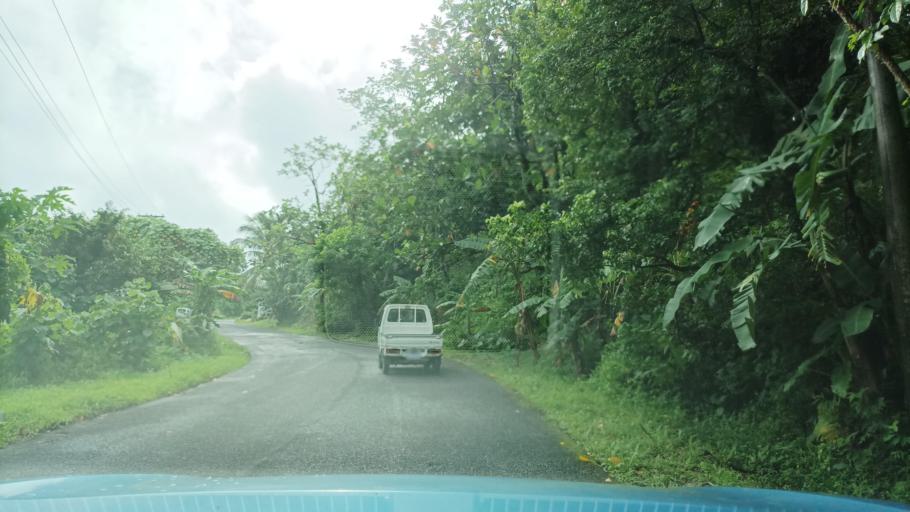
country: FM
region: Pohnpei
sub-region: Kolonia Municipality
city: Kolonia
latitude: 6.9694
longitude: 158.2586
